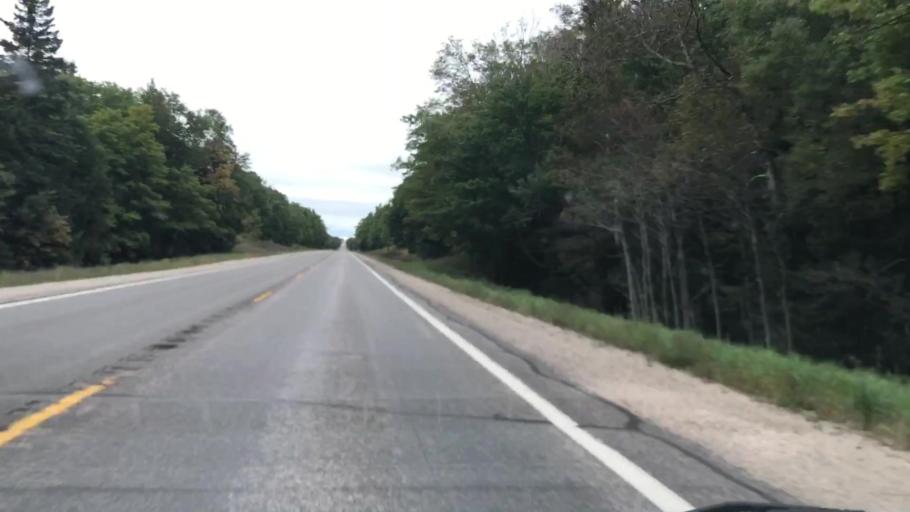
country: US
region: Michigan
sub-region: Luce County
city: Newberry
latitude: 46.2449
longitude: -85.5723
